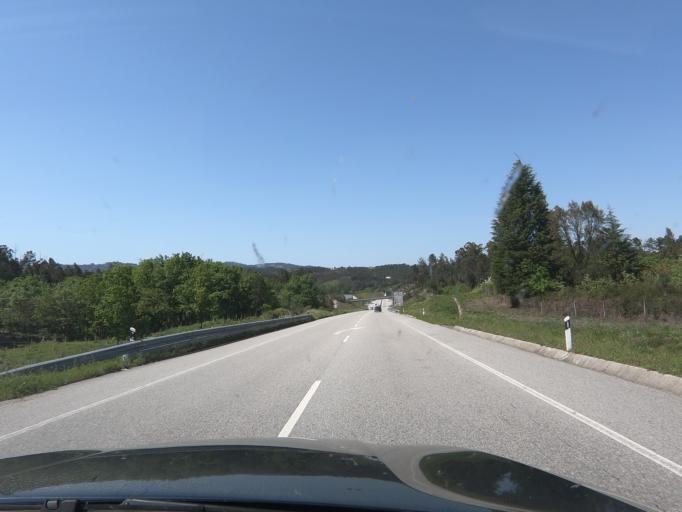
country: PT
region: Coimbra
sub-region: Vila Nova de Poiares
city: Poiares
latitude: 40.1697
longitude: -8.2664
